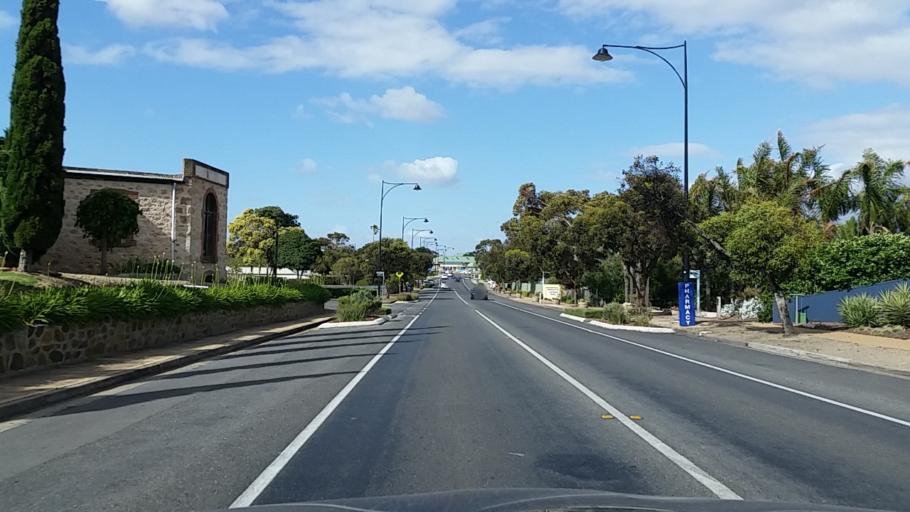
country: AU
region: South Australia
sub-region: Alexandrina
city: Port Elliot
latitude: -35.5093
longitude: 138.7069
